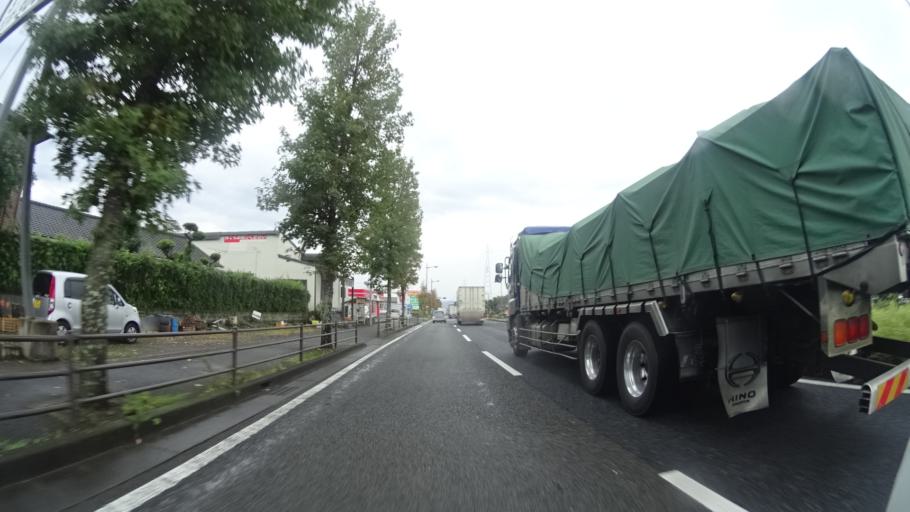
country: JP
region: Kagoshima
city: Kajiki
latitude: 31.7088
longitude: 130.6150
